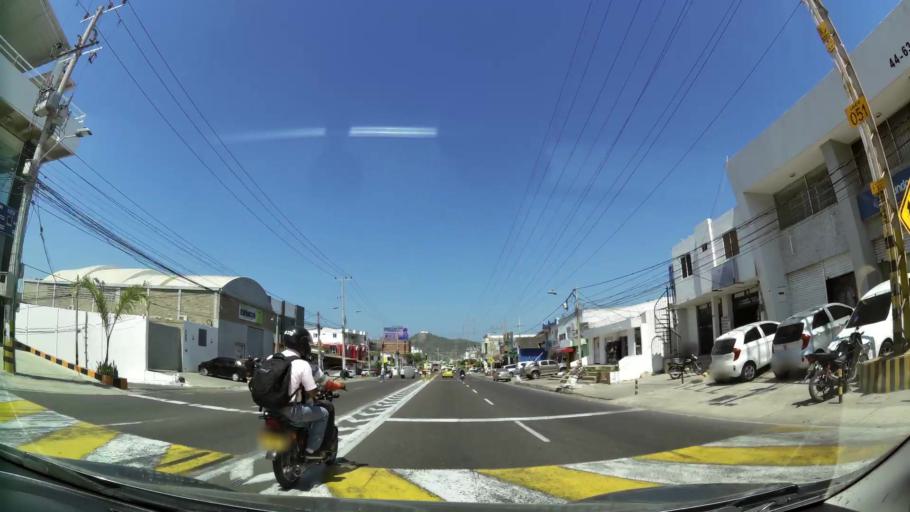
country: CO
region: Bolivar
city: Cartagena
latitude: 10.4013
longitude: -75.5193
